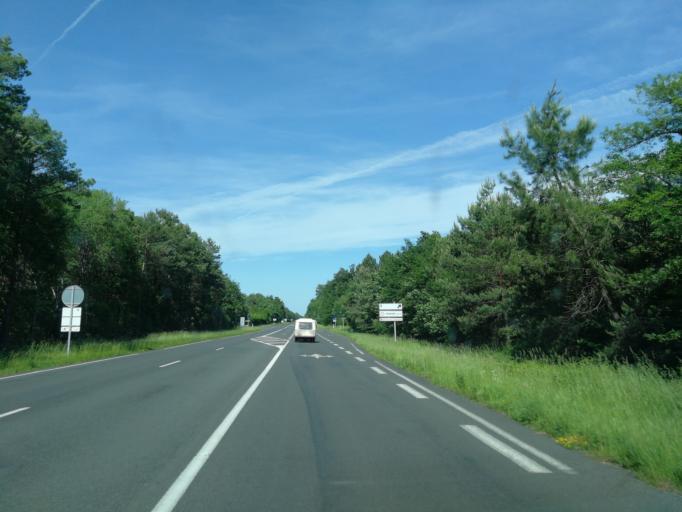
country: FR
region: Centre
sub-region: Departement d'Indre-et-Loire
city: Cheille
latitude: 47.2213
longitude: 0.3759
